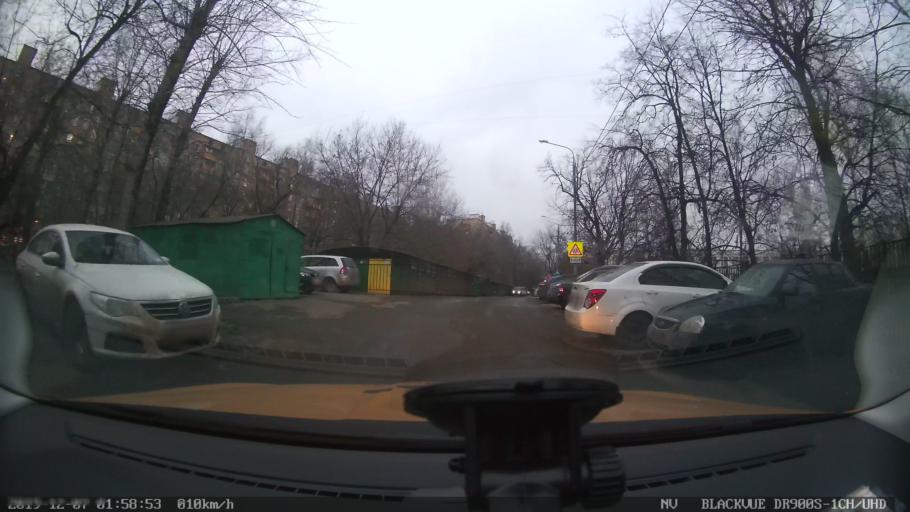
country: RU
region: Moskovskaya
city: Bol'shaya Setun'
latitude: 55.7233
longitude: 37.4264
